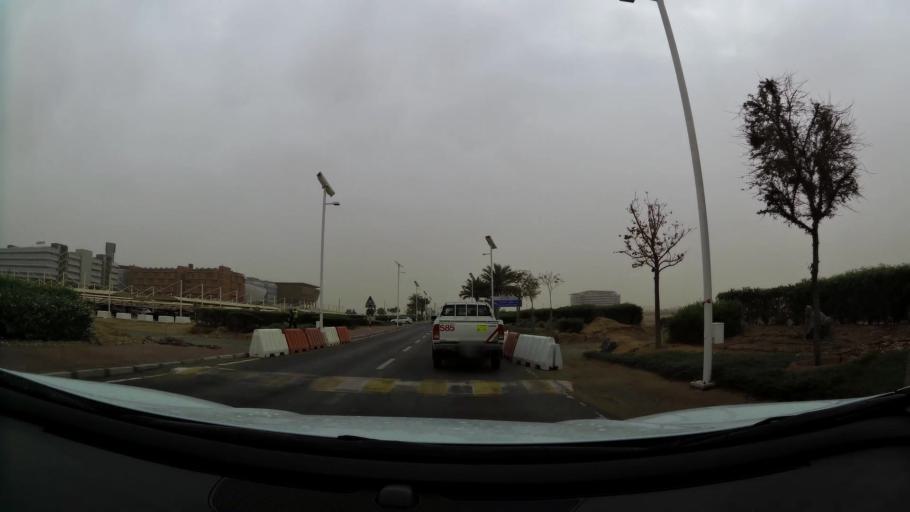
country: AE
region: Abu Dhabi
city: Abu Dhabi
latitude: 24.4332
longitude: 54.6140
